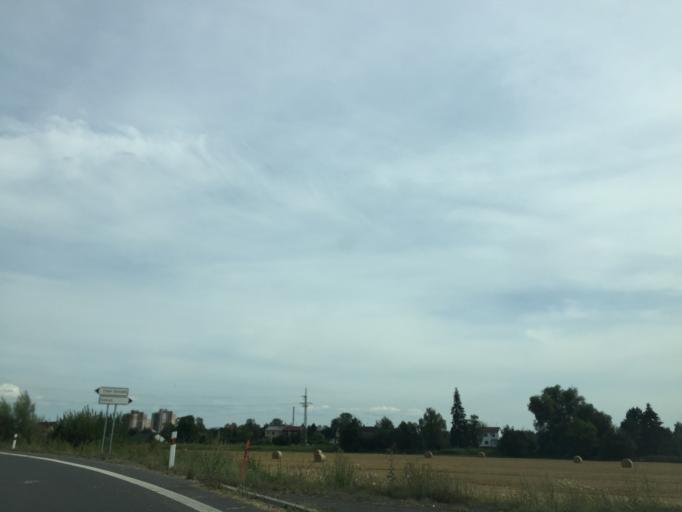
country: CZ
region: Moravskoslezsky
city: Stary Bohumin
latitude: 49.9115
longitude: 18.3424
